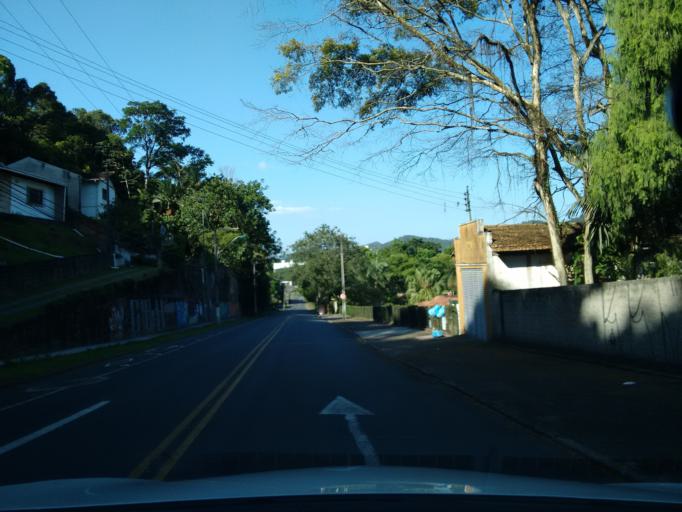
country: BR
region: Santa Catarina
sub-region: Blumenau
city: Blumenau
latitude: -26.9058
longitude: -49.0701
